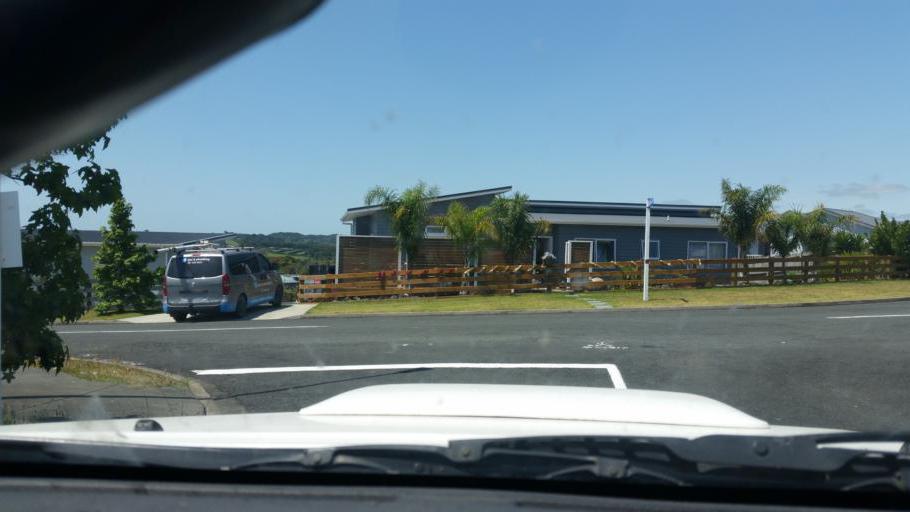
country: NZ
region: Auckland
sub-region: Auckland
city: Wellsford
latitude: -36.1242
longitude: 174.5718
